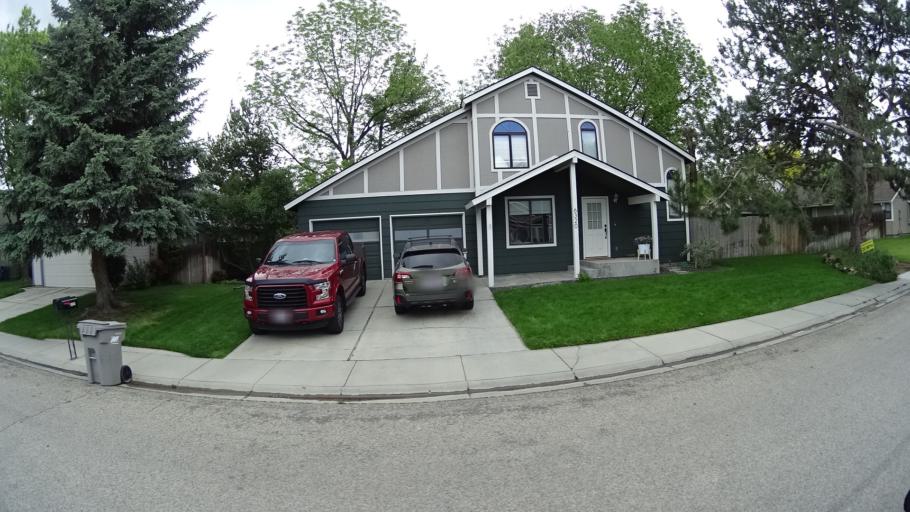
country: US
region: Idaho
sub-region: Ada County
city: Garden City
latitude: 43.6776
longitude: -116.2726
